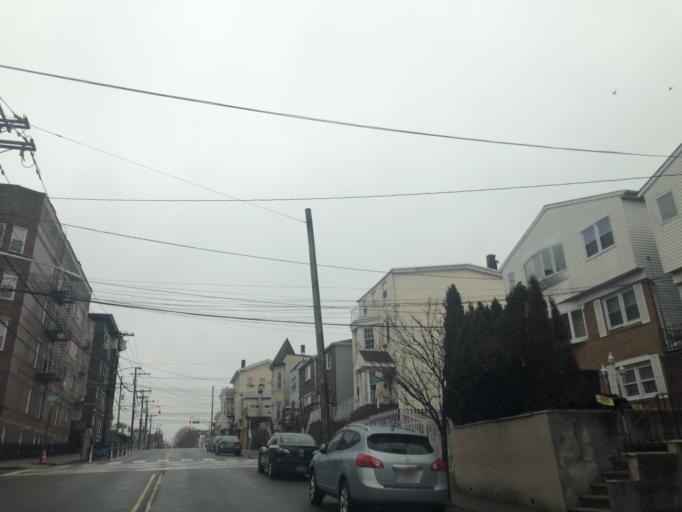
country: US
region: New Jersey
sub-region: Hudson County
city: Hoboken
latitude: 40.7487
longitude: -74.0399
